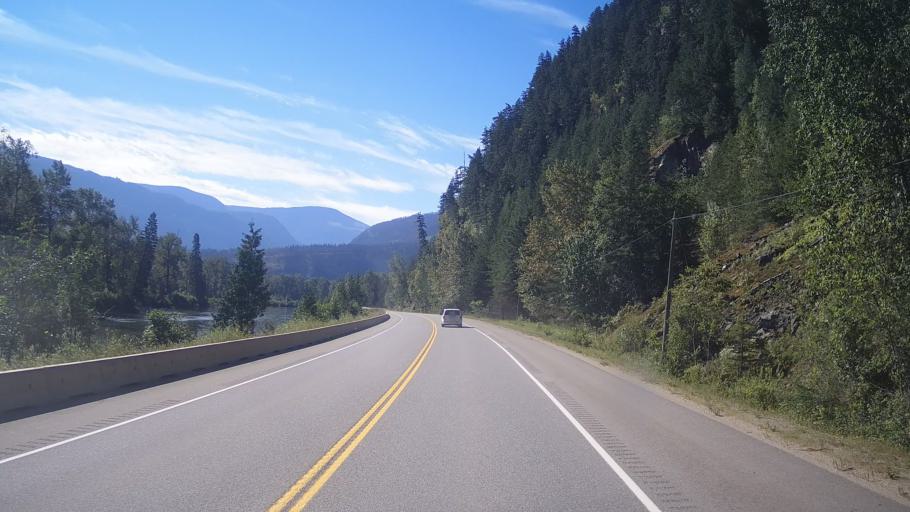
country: CA
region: British Columbia
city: Kamloops
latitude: 51.4779
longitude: -120.1826
